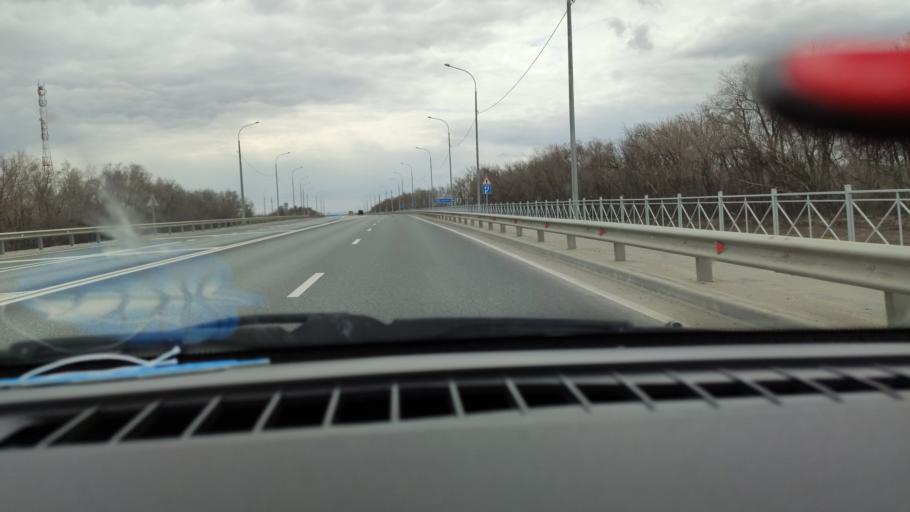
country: RU
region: Saratov
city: Yelshanka
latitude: 51.8914
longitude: 46.5247
